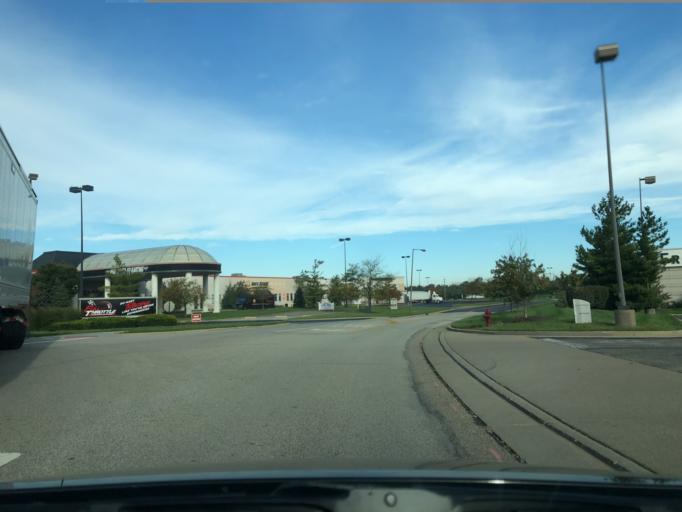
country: US
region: Ohio
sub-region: Hamilton County
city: Glendale
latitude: 39.2899
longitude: -84.4533
